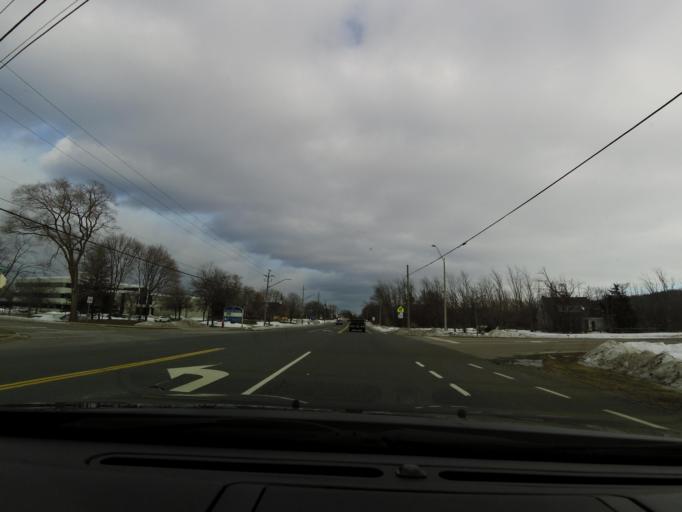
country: CA
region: Ontario
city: Hamilton
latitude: 43.2119
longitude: -79.6931
